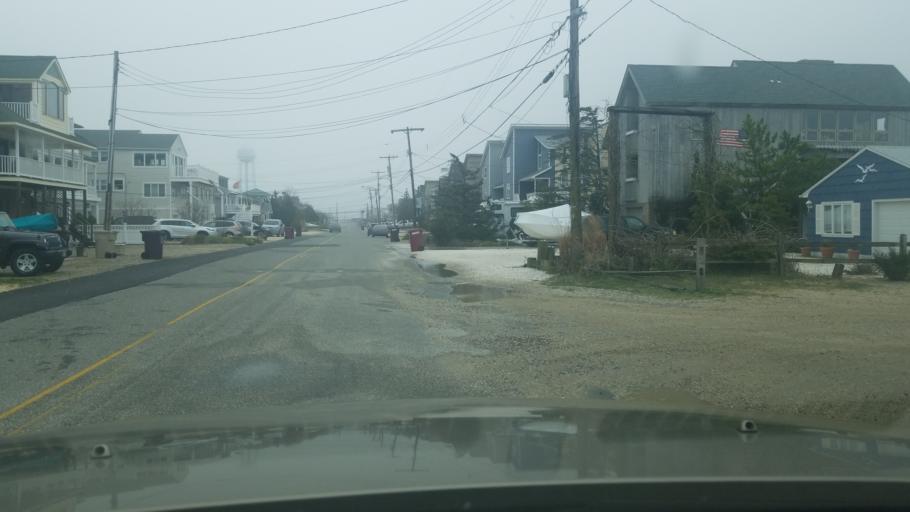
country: US
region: New Jersey
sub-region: Ocean County
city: Seaside Park
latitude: 39.9062
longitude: -74.0865
